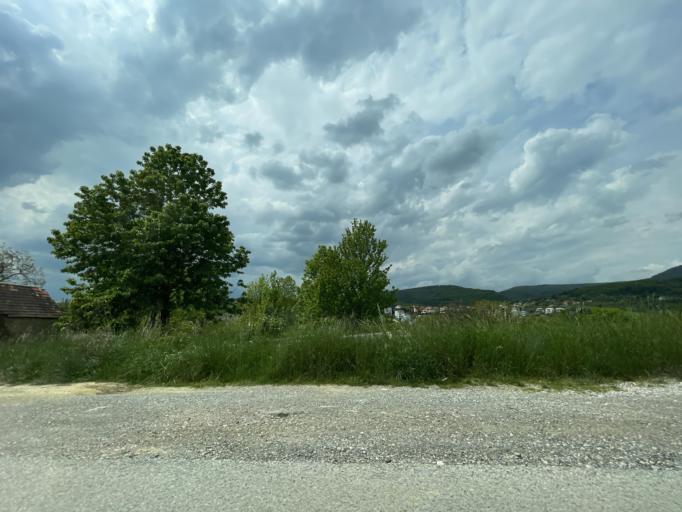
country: HR
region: Grad Zagreb
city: Zagreb
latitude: 45.8461
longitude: 15.9455
